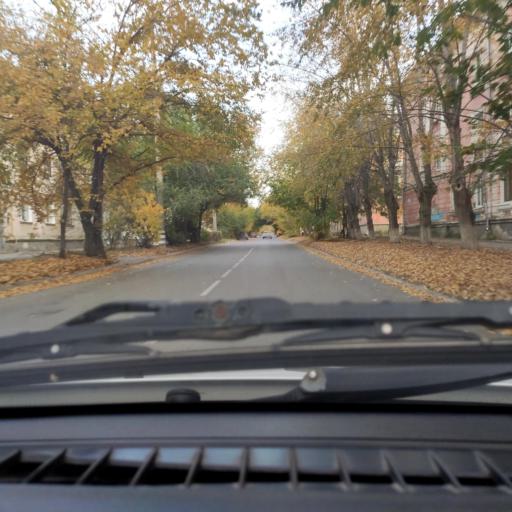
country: RU
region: Samara
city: Zhigulevsk
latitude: 53.4657
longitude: 49.5293
